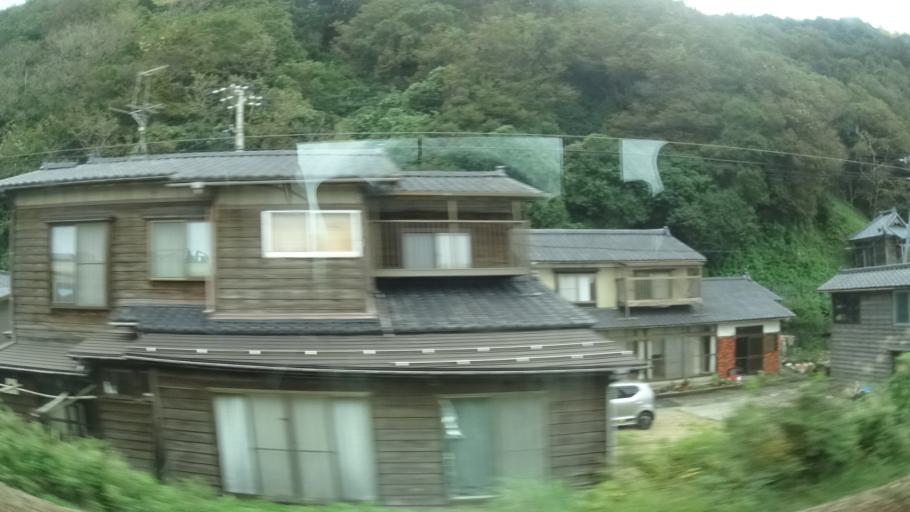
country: JP
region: Niigata
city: Murakami
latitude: 38.4604
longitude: 139.4986
